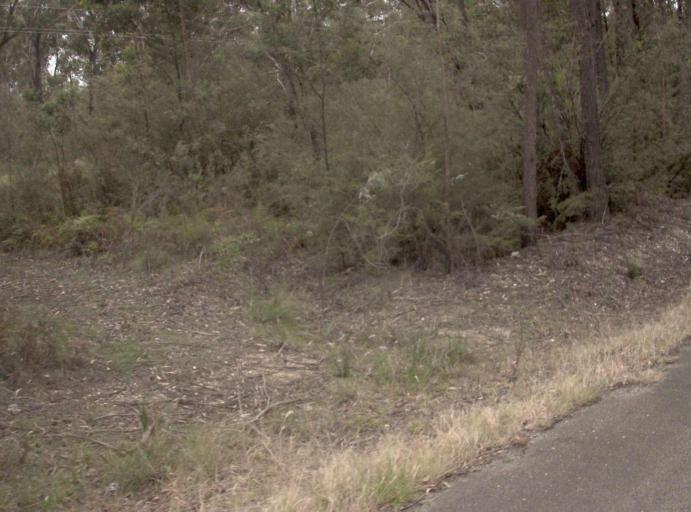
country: AU
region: Victoria
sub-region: East Gippsland
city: Lakes Entrance
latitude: -37.7293
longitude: 147.9186
